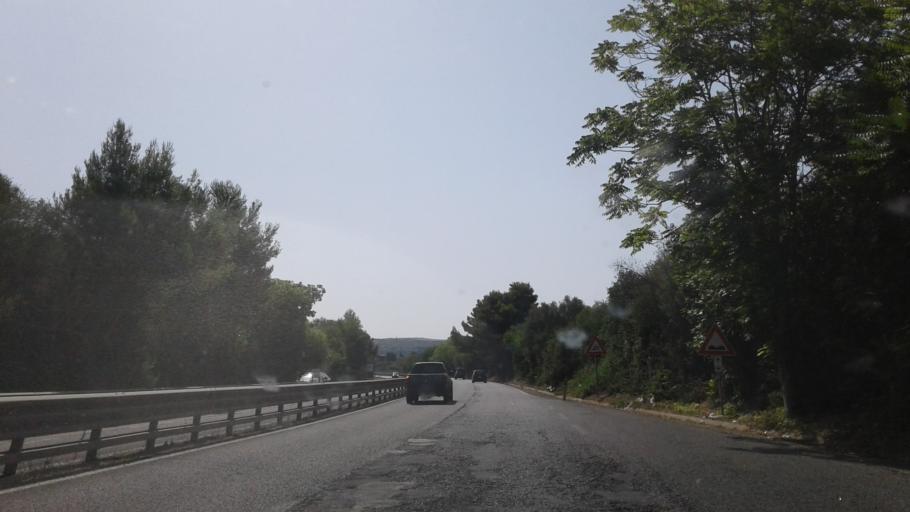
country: IT
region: Sardinia
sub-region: Provincia di Sassari
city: Sassari
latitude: 40.7043
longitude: 8.5523
